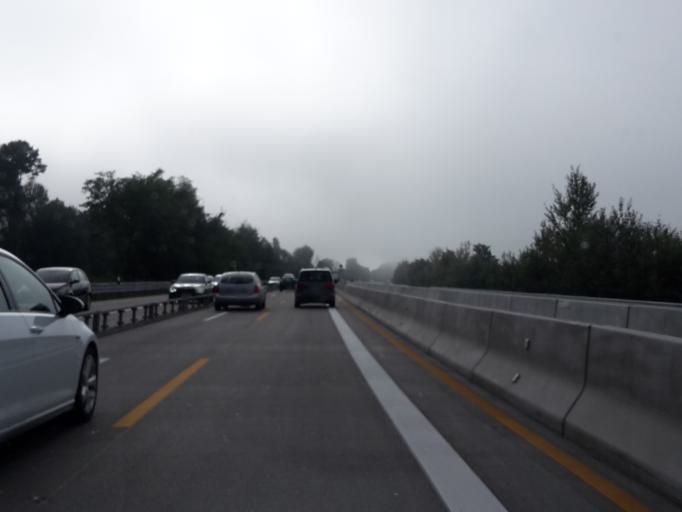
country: DE
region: Baden-Wuerttemberg
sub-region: Karlsruhe Region
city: Laudenbach
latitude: 49.6102
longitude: 8.6286
